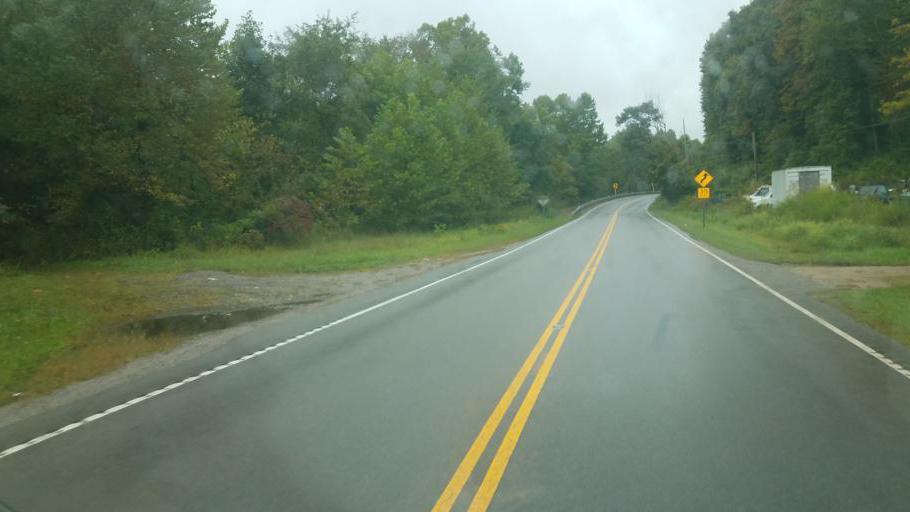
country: US
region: Ohio
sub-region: Jackson County
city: Oak Hill
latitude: 38.8256
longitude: -82.6627
